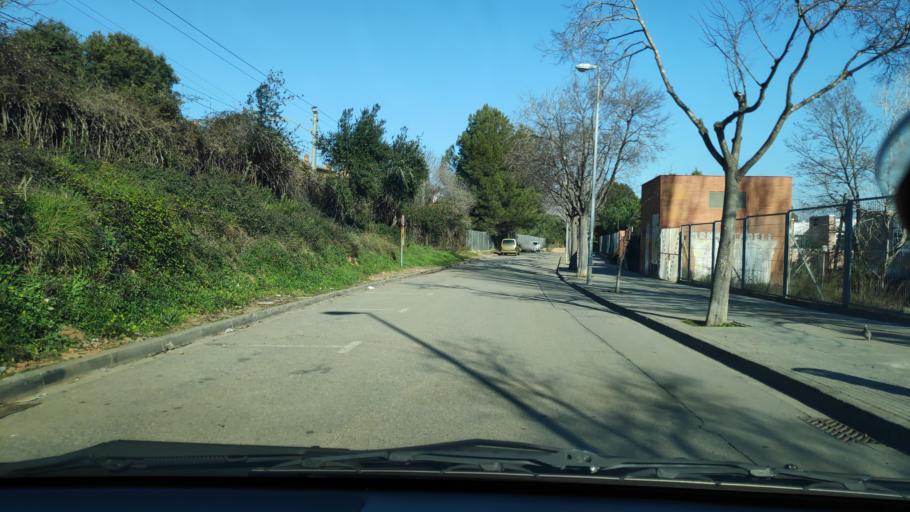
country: ES
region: Catalonia
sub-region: Provincia de Barcelona
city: Sant Cugat del Valles
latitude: 41.4604
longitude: 2.0698
